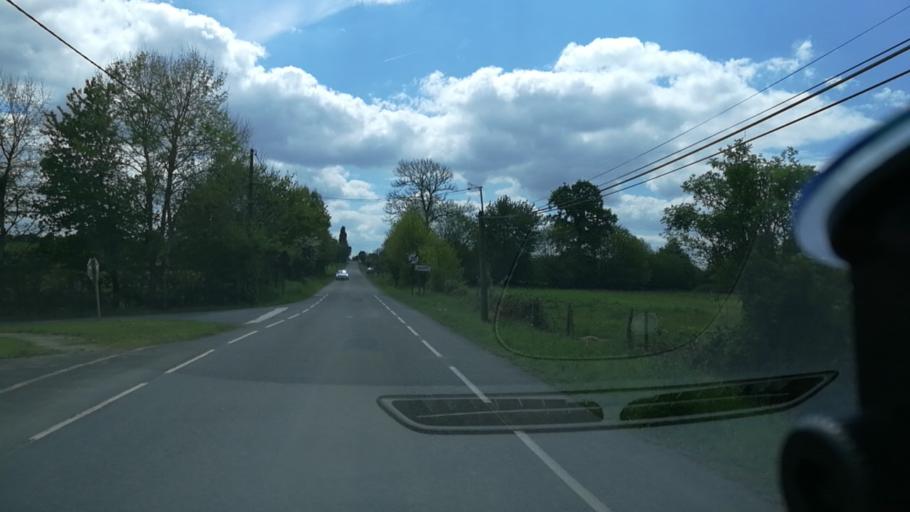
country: FR
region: Brittany
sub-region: Departement d'Ille-et-Vilaine
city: Retiers
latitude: 47.9067
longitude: -1.3798
